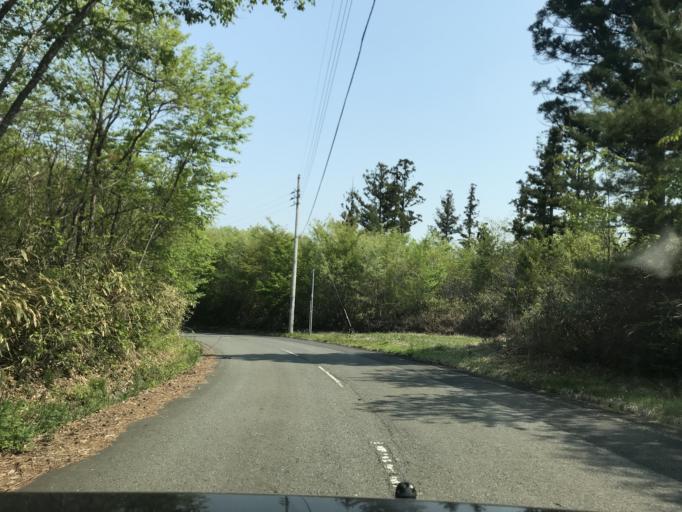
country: JP
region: Iwate
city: Ichinoseki
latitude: 38.8892
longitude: 141.0659
